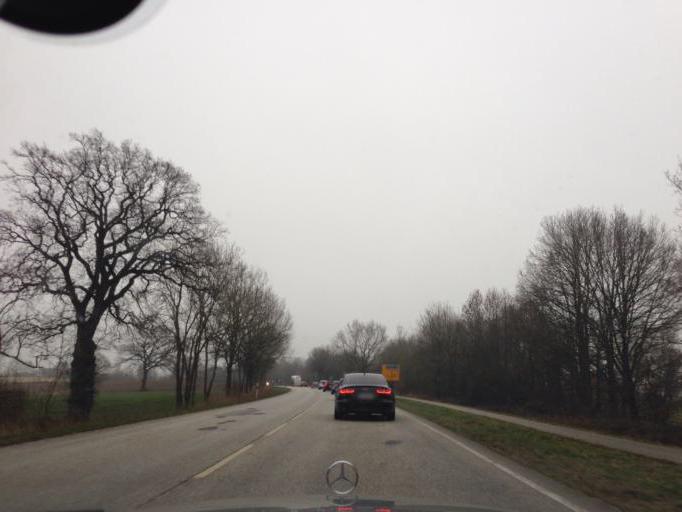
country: DE
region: Schleswig-Holstein
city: Warnau
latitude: 54.1886
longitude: 10.1658
